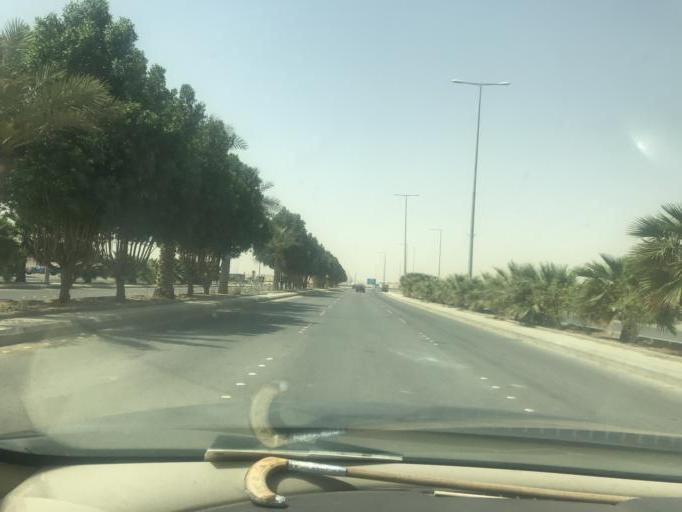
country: SA
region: Ar Riyad
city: Riyadh
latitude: 24.8061
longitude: 46.5810
